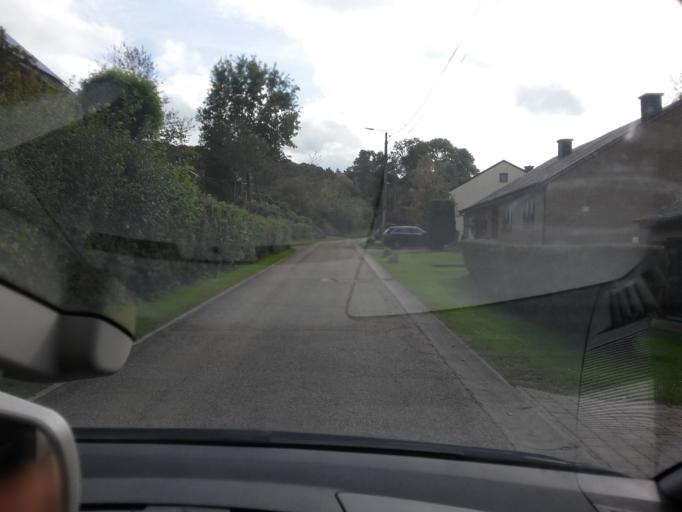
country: BE
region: Wallonia
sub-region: Province du Luxembourg
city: Attert
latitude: 49.7225
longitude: 5.7914
